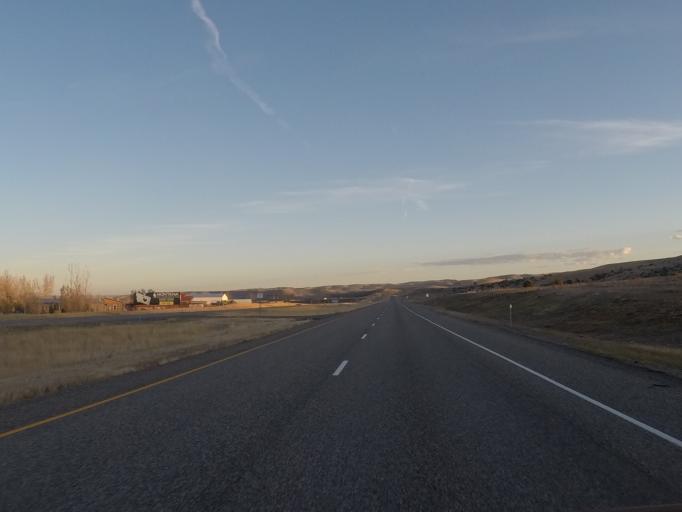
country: US
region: Montana
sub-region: Sweet Grass County
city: Big Timber
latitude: 45.7649
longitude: -109.7902
